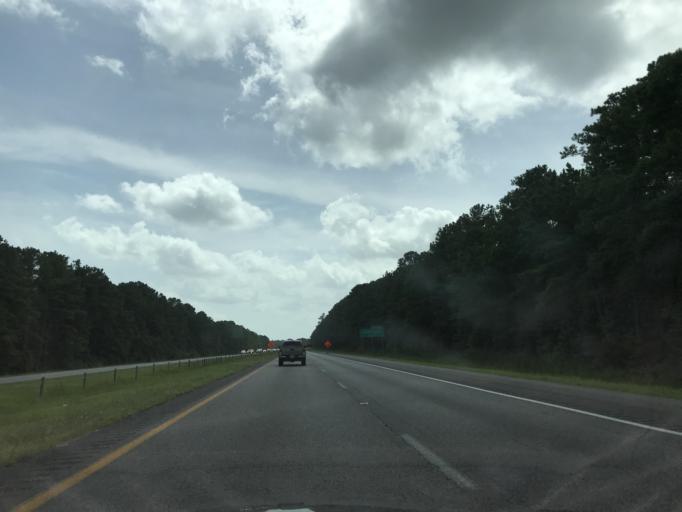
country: US
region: North Carolina
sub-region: New Hanover County
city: Castle Hayne
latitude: 34.3806
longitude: -77.8814
